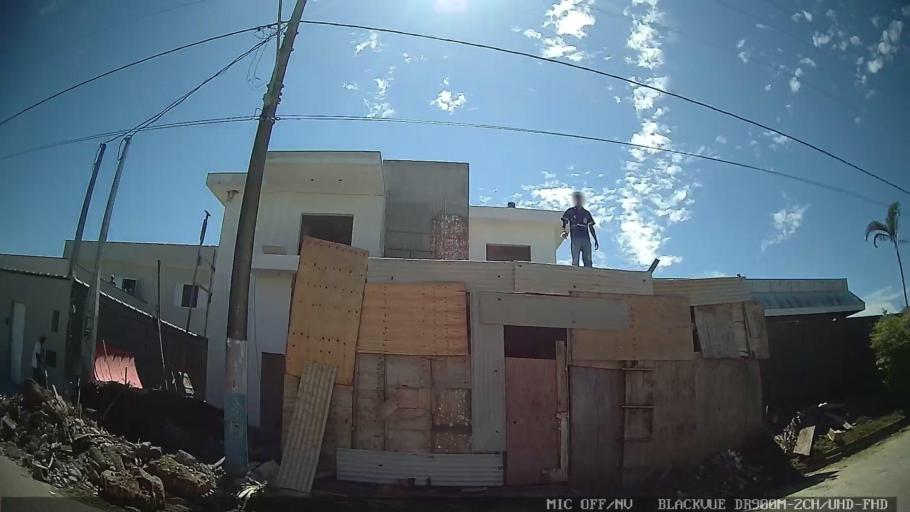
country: BR
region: Sao Paulo
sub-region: Iguape
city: Iguape
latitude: -24.7139
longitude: -47.5602
